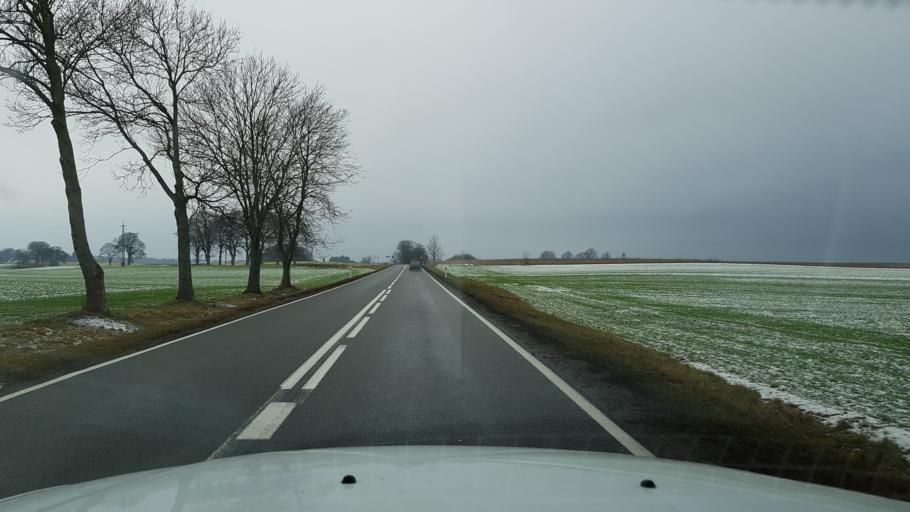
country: PL
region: West Pomeranian Voivodeship
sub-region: Powiat drawski
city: Czaplinek
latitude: 53.5560
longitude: 16.2185
